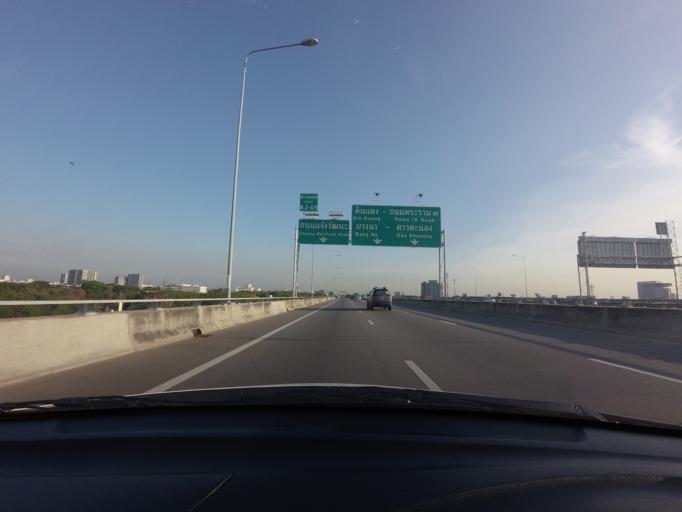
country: TH
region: Bangkok
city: Lak Si
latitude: 13.9087
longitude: 100.5442
